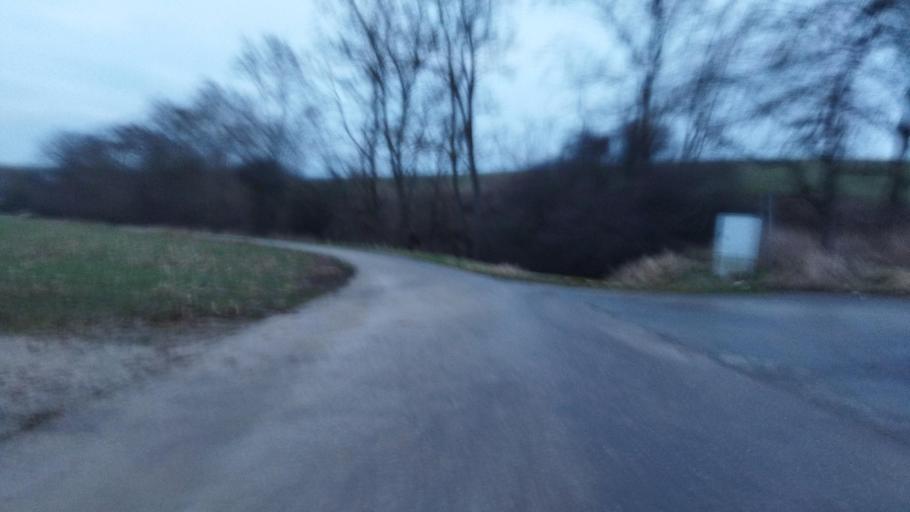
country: DE
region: Baden-Wuerttemberg
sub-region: Regierungsbezirk Stuttgart
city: Bad Rappenau
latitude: 49.2070
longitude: 9.0990
